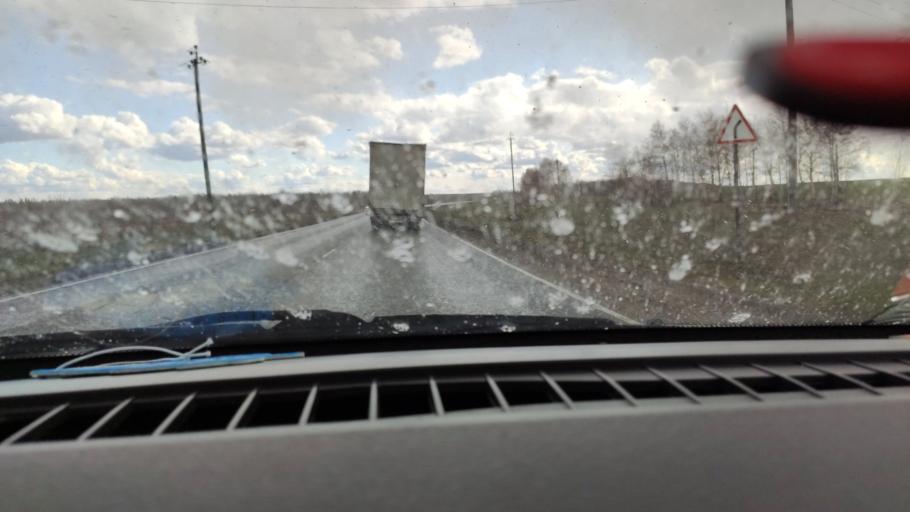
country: RU
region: Saratov
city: Balakovo
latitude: 52.1109
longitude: 47.7485
